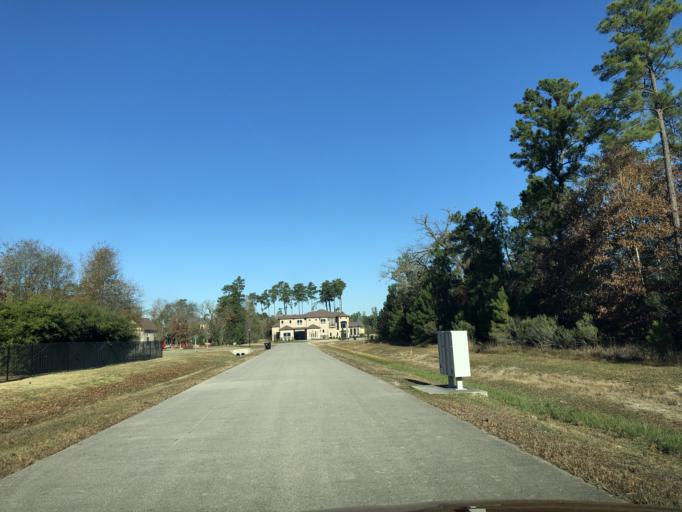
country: US
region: Texas
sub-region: Montgomery County
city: Porter Heights
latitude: 30.0700
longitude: -95.3186
